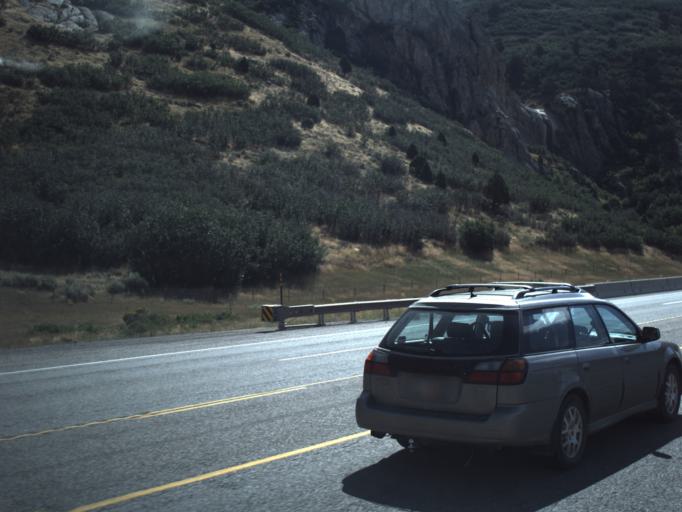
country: US
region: Utah
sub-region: Utah County
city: Mapleton
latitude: 40.0158
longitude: -111.4938
